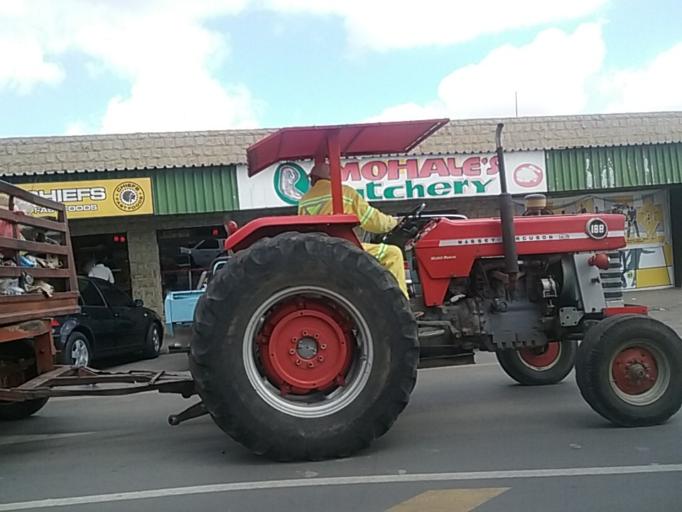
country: LS
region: Berea
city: Teyateyaneng
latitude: -29.1483
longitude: 27.7484
